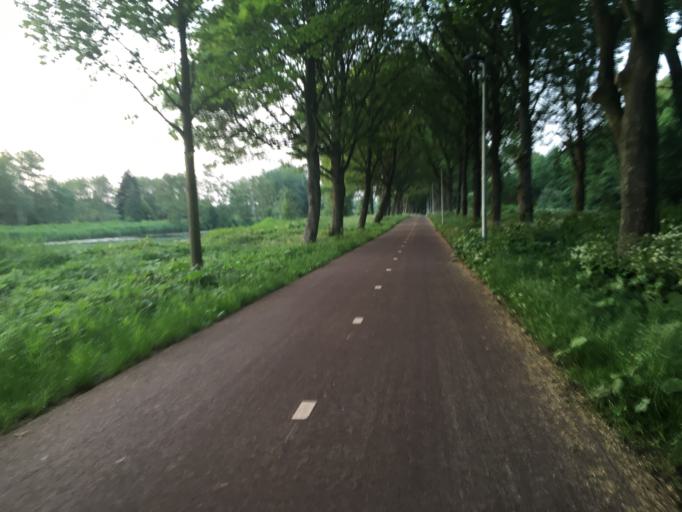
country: NL
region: South Holland
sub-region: Gemeente Schiedam
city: Schiedam
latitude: 51.9135
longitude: 4.3738
